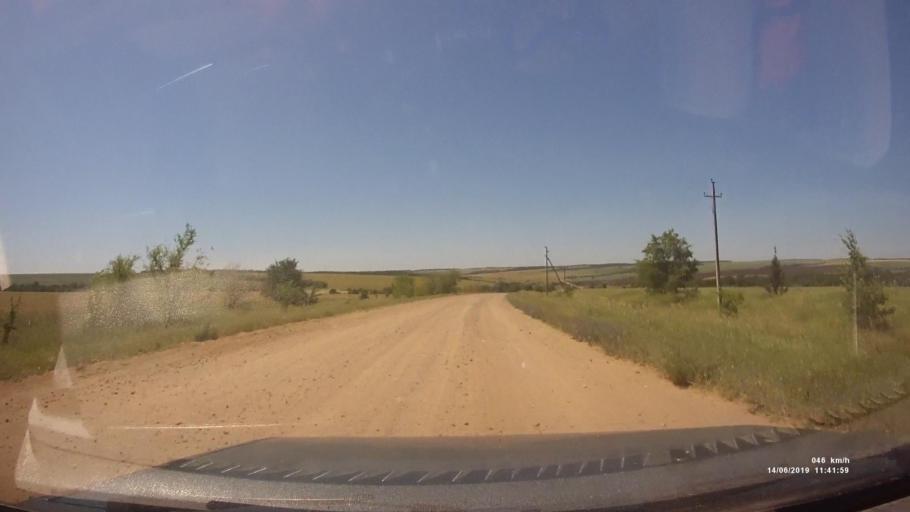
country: RU
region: Rostov
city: Kazanskaya
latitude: 49.8609
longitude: 41.3476
